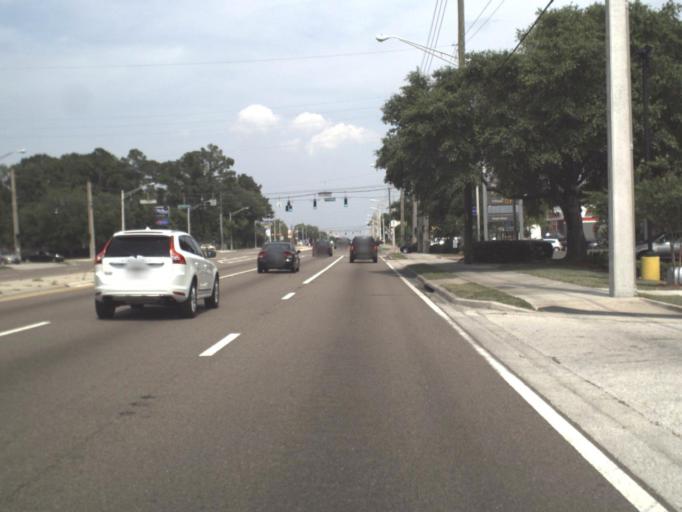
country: US
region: Florida
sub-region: Clay County
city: Bellair-Meadowbrook Terrace
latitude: 30.2481
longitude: -81.7783
